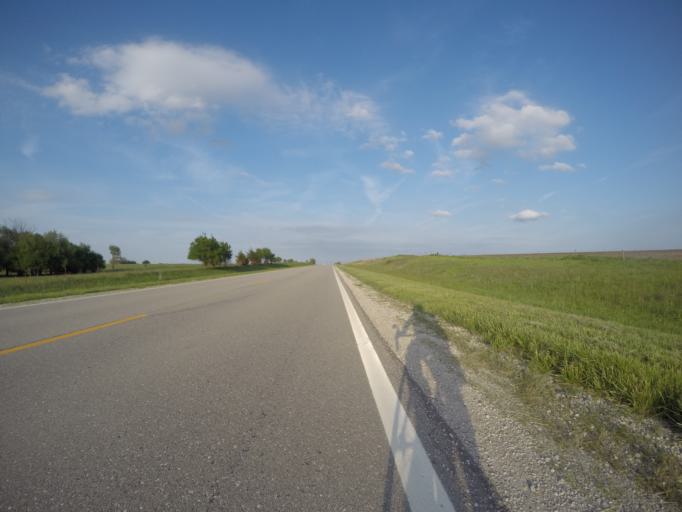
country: US
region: Kansas
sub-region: Pottawatomie County
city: Westmoreland
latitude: 39.4284
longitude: -96.5445
